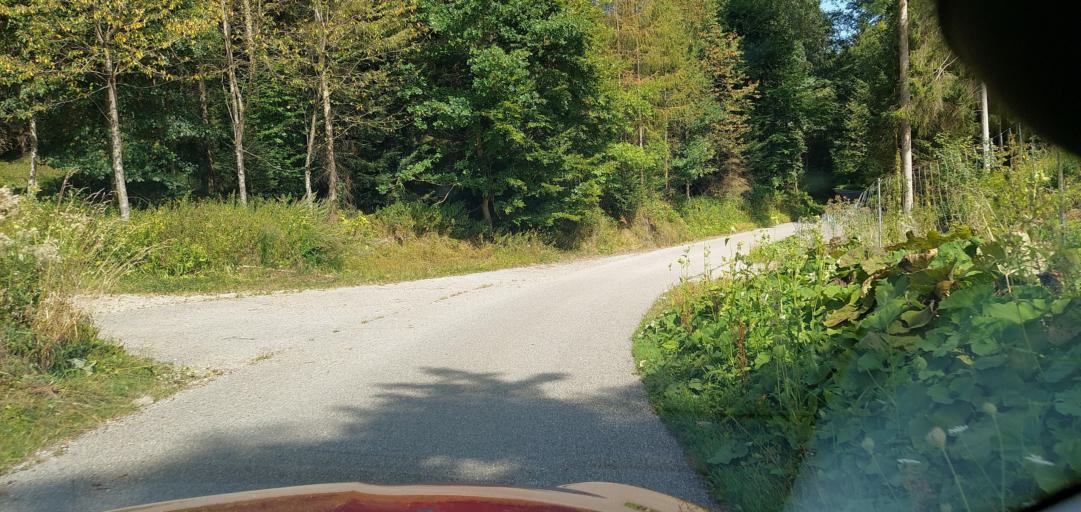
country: AT
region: Upper Austria
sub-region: Wels-Land
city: Pennewang
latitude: 48.1394
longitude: 13.8565
